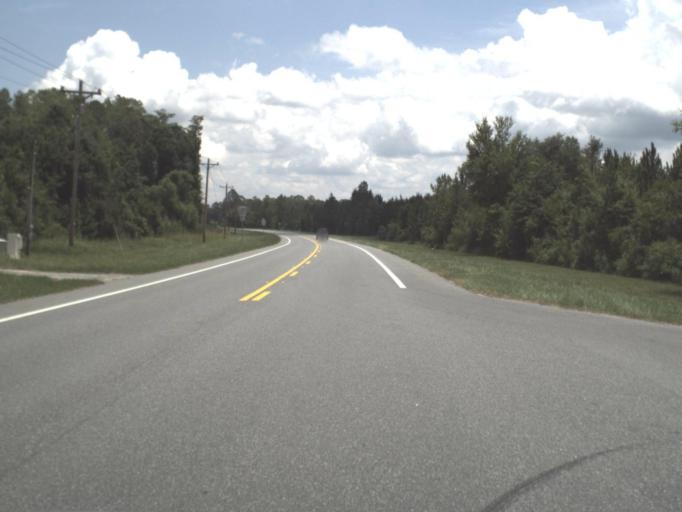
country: US
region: Florida
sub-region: Union County
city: Lake Butler
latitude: 30.0129
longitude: -82.4248
